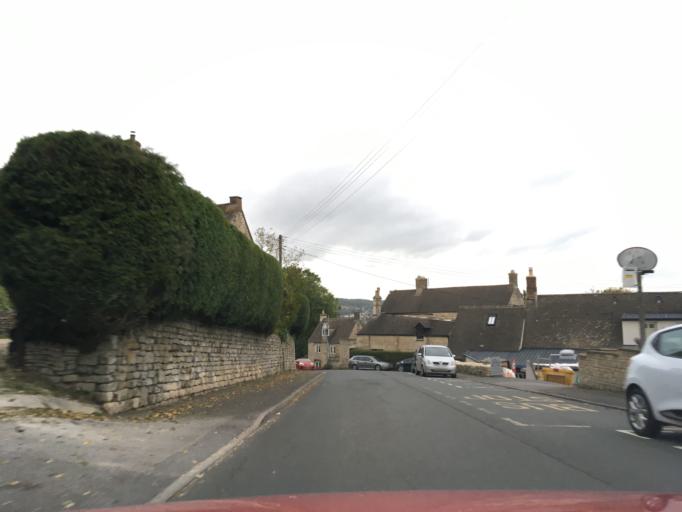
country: GB
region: England
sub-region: Gloucestershire
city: Stroud
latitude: 51.7334
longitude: -2.2403
